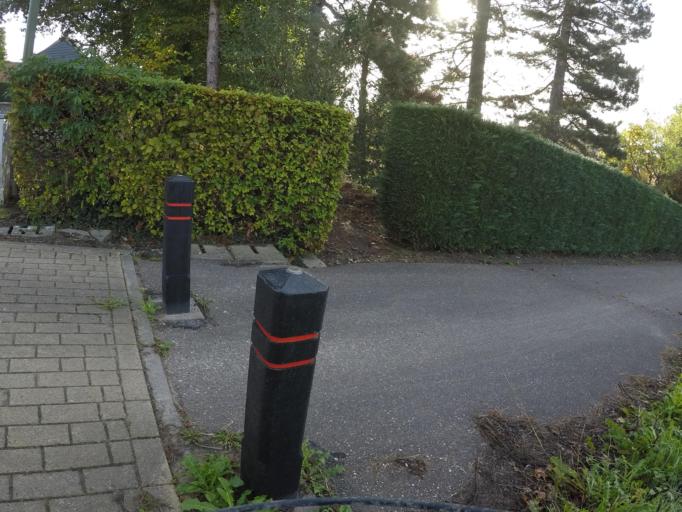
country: BE
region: Flanders
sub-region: Provincie Vlaams-Brabant
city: Begijnendijk
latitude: 50.9869
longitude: 4.7780
